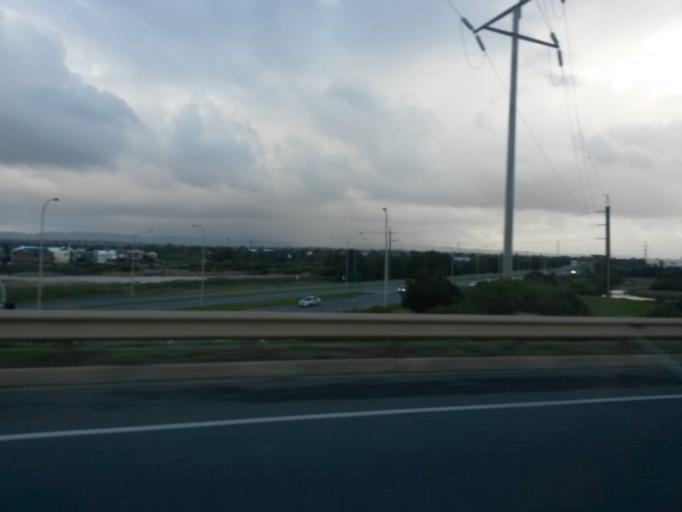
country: AU
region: South Australia
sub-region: Port Adelaide Enfield
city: Enfield
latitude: -34.8124
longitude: 138.5968
